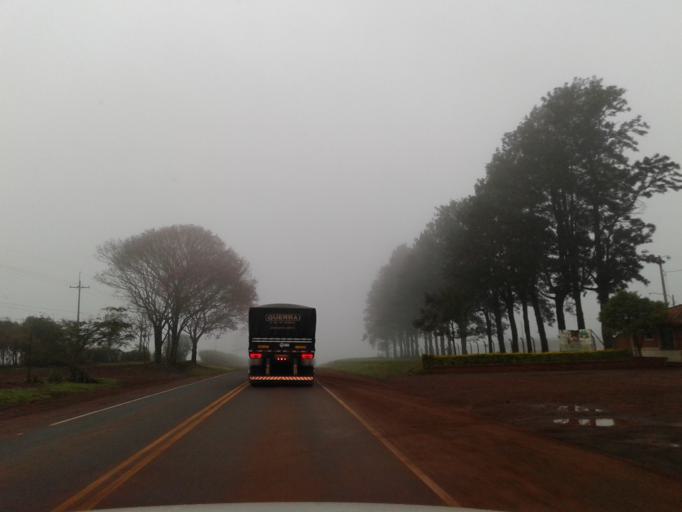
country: PY
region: Itapua
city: Pirapo
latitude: -26.8636
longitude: -55.4528
